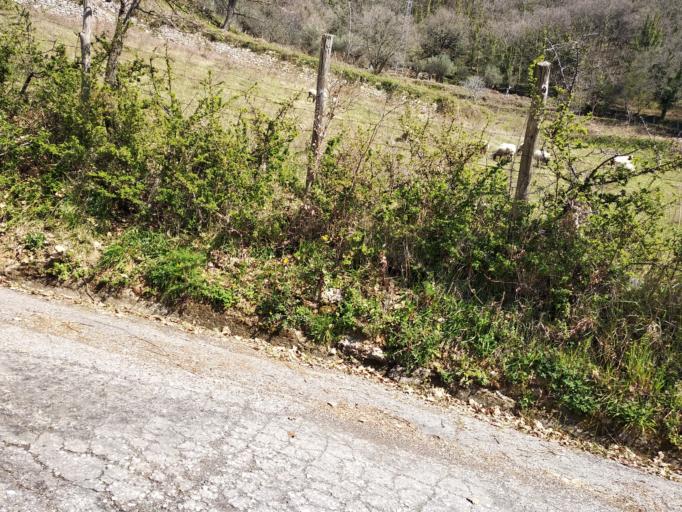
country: IT
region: Calabria
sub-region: Provincia di Cosenza
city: Altilia
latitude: 39.1280
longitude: 16.2477
